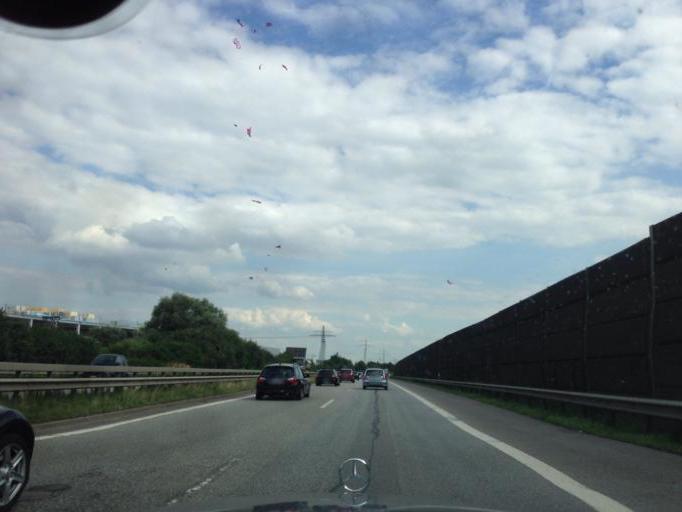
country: DE
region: Hamburg
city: Rothenburgsort
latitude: 53.5018
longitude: 10.0865
